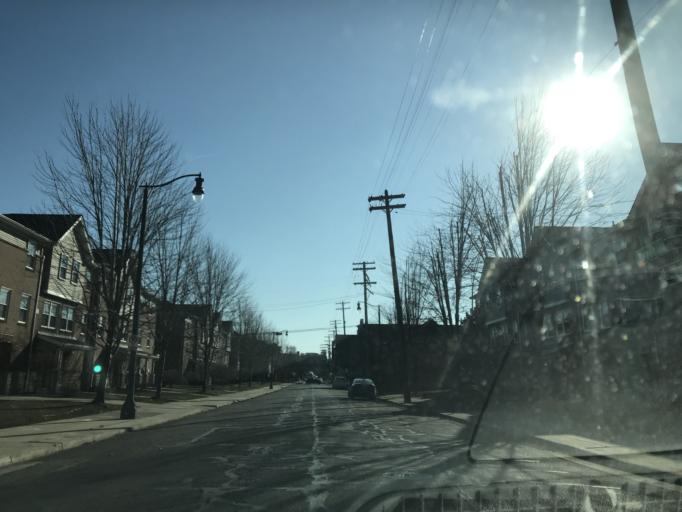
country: US
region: Michigan
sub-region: Wayne County
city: Hamtramck
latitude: 42.3644
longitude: -83.0622
